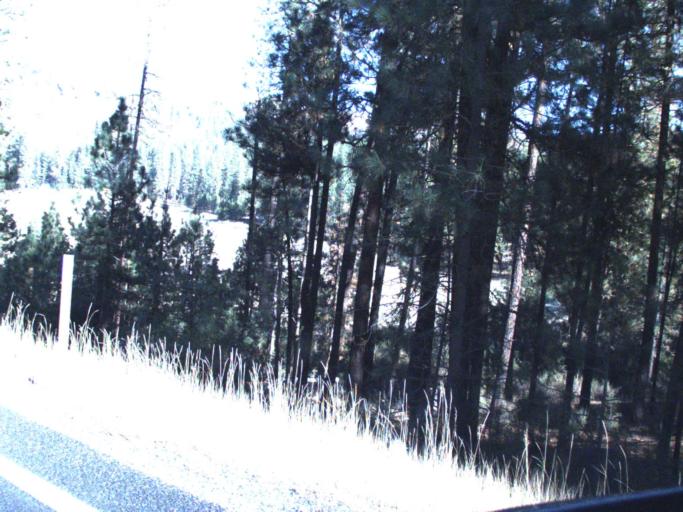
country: US
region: Washington
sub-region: Lincoln County
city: Davenport
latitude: 48.0179
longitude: -118.2372
